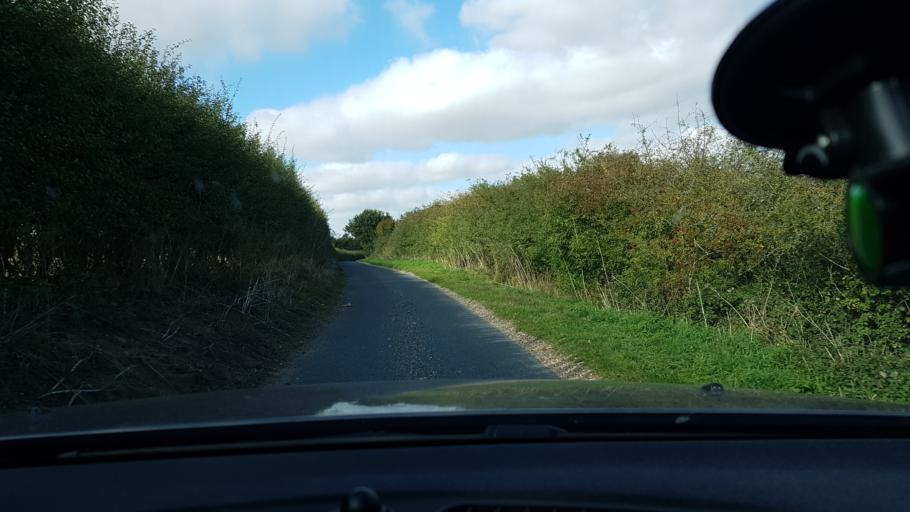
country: GB
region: England
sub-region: West Berkshire
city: Kintbury
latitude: 51.4242
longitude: -1.4482
